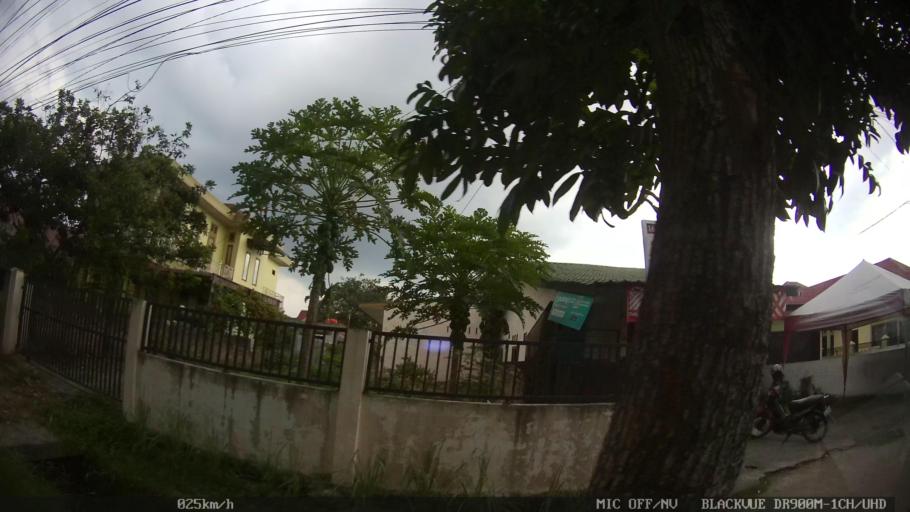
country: ID
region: North Sumatra
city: Sunggal
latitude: 3.5233
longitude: 98.6156
